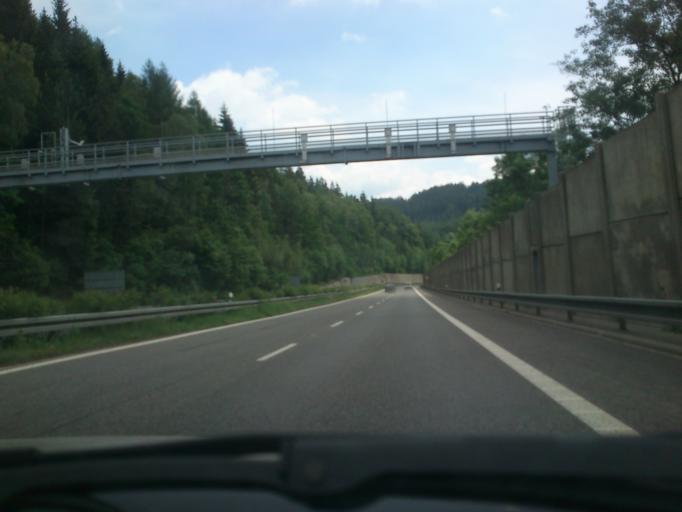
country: CZ
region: Liberecky
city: Hodkovice nad Mohelkou
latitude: 50.6931
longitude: 15.1056
